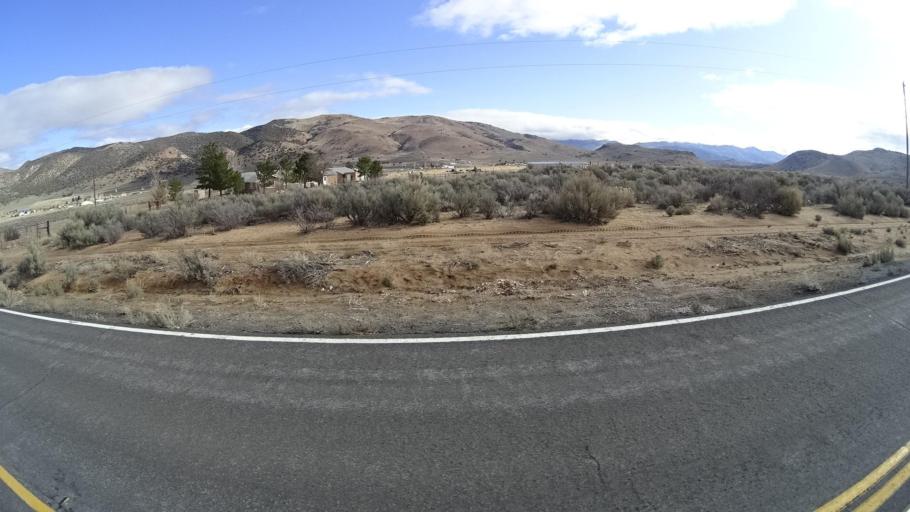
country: US
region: Nevada
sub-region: Washoe County
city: Cold Springs
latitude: 39.8901
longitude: -119.9766
